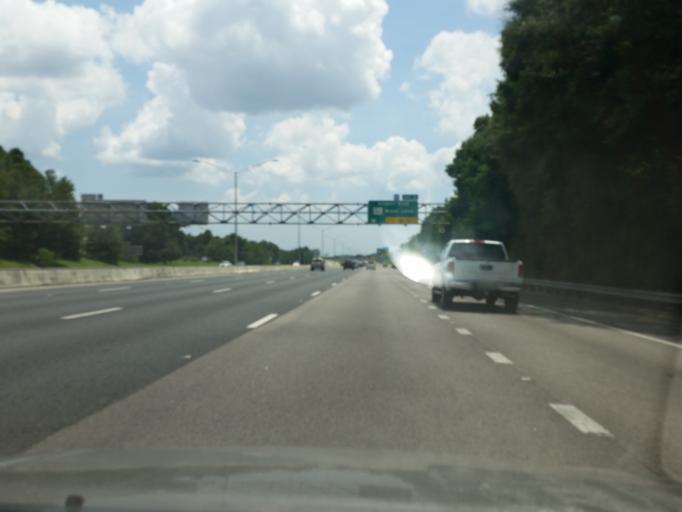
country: US
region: Florida
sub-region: Escambia County
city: Brent
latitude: 30.4929
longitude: -87.2304
